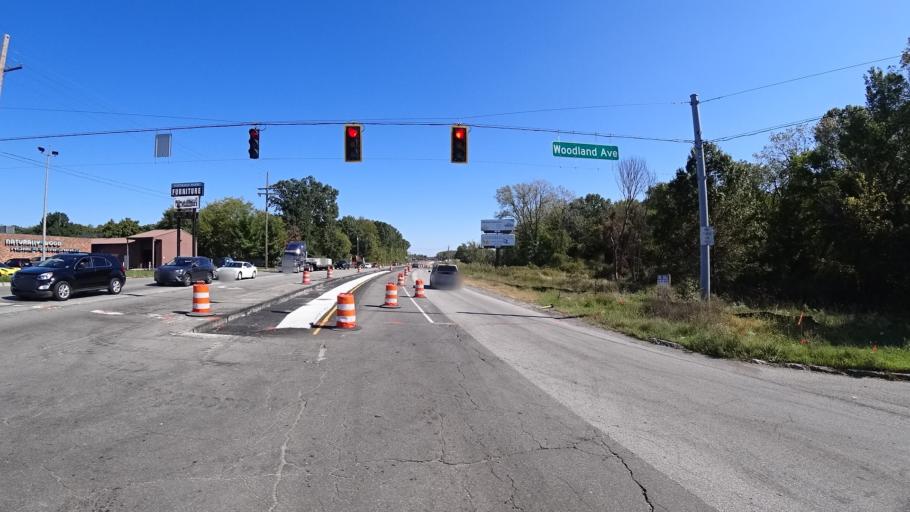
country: US
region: Indiana
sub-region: LaPorte County
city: Trail Creek
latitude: 41.6873
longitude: -86.8744
